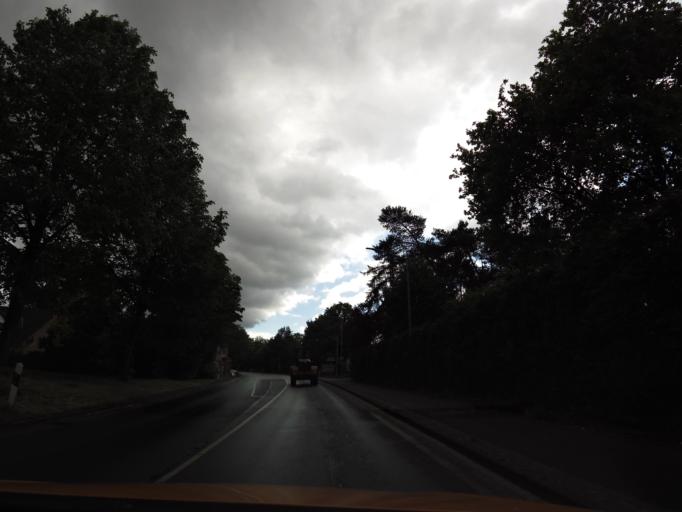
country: DE
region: Lower Saxony
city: Hude
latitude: 53.1020
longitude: 8.4772
